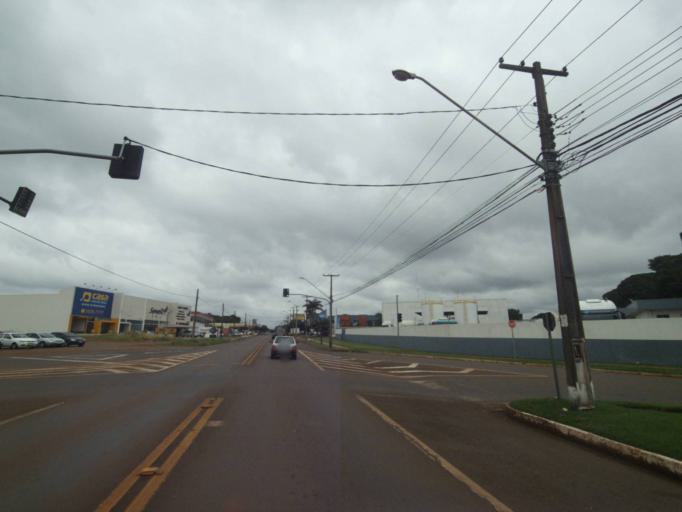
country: BR
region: Parana
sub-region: Campo Mourao
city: Campo Mourao
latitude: -24.0277
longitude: -52.3652
